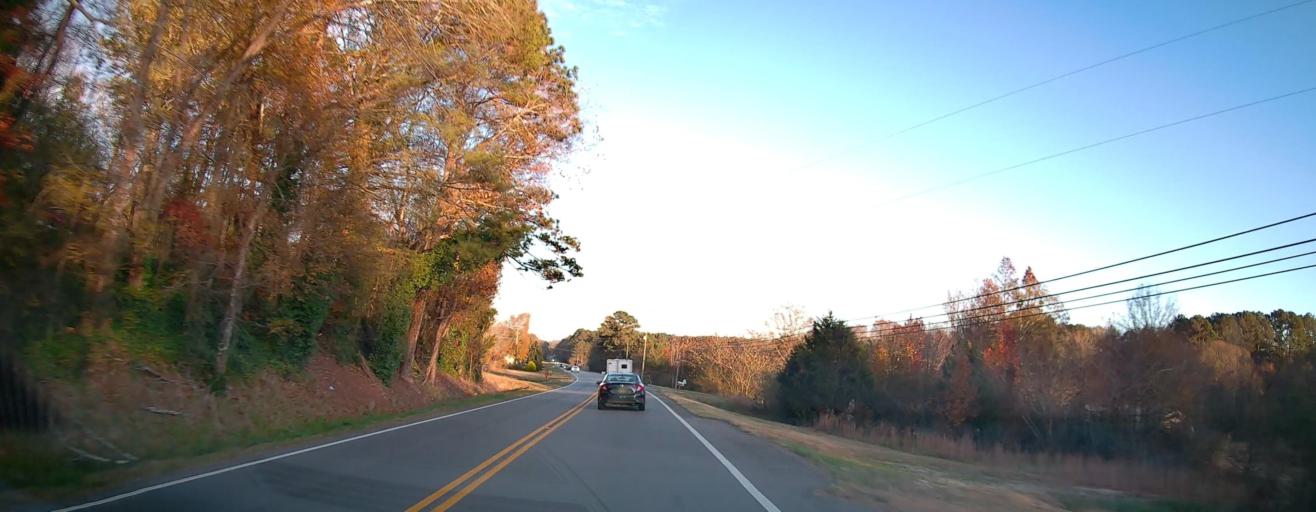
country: US
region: Alabama
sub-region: Etowah County
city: Attalla
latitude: 34.0397
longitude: -86.1409
